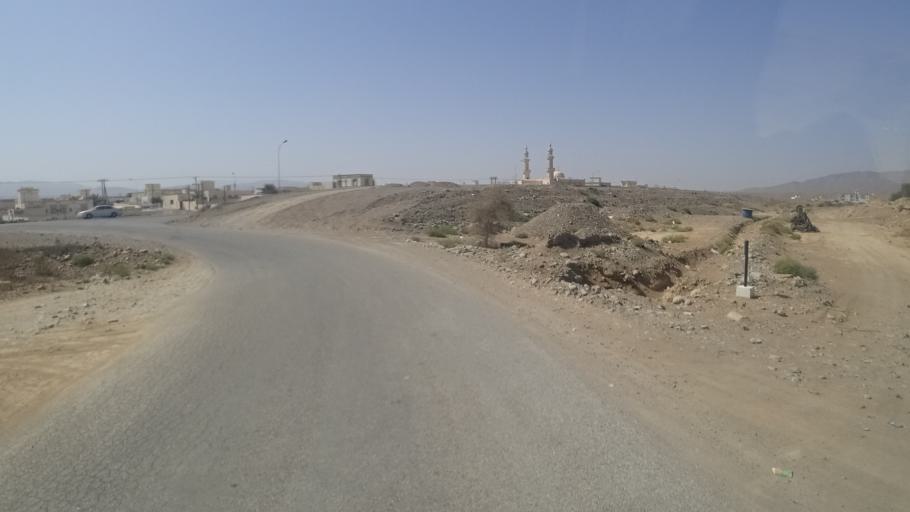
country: OM
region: Ash Sharqiyah
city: Sur
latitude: 22.4519
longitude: 59.3753
